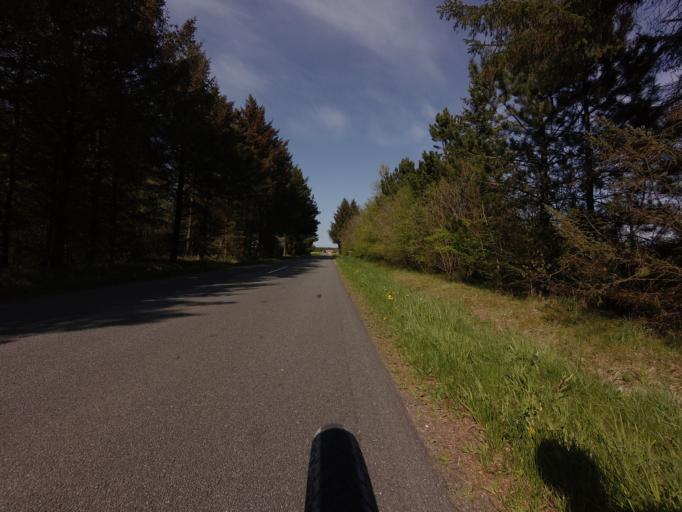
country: DK
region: North Denmark
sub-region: Jammerbugt Kommune
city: Pandrup
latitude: 57.2282
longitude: 9.6051
